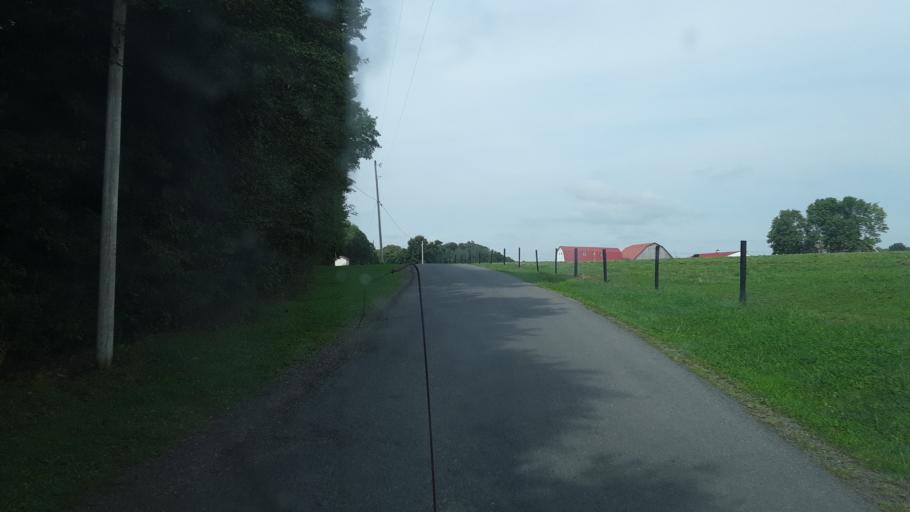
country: US
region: Pennsylvania
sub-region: Jefferson County
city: Punxsutawney
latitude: 40.9392
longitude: -79.0606
